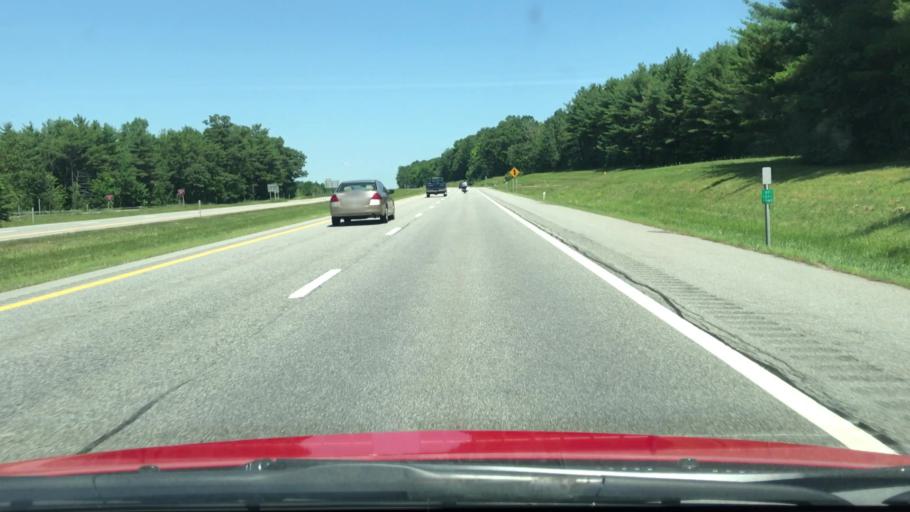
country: US
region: New York
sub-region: Essex County
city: Keeseville
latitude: 44.4453
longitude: -73.4905
